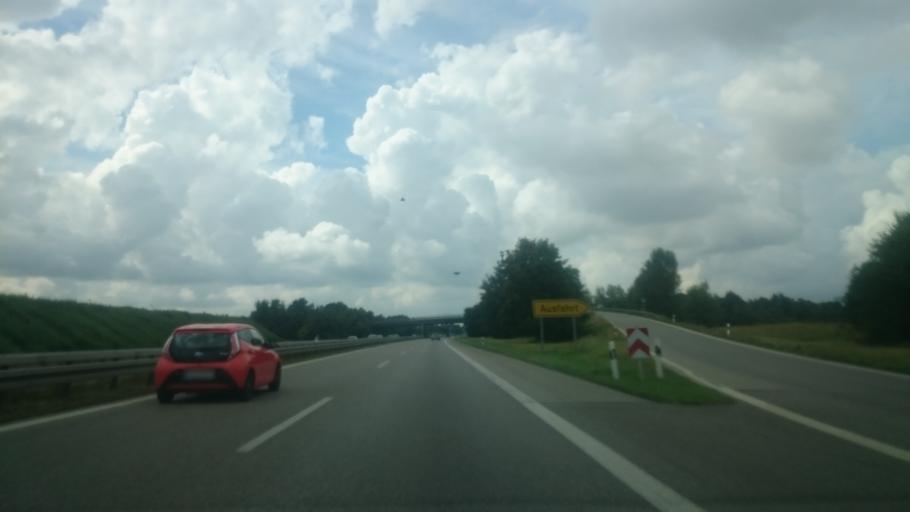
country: DE
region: Bavaria
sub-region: Swabia
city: Kleinaitingen
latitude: 48.2033
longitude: 10.8553
